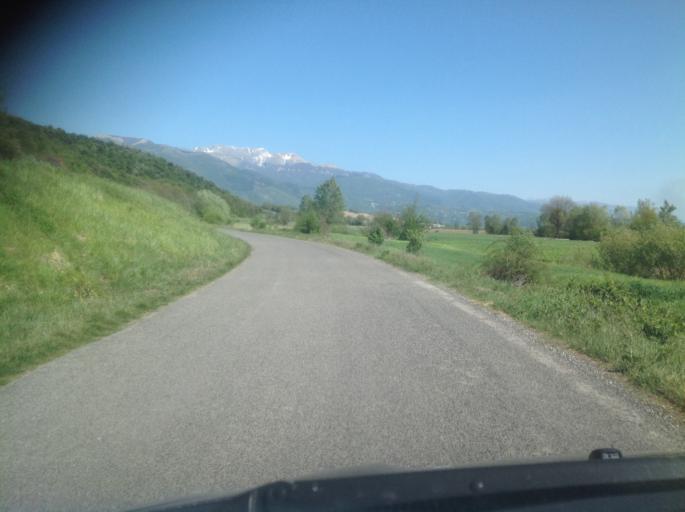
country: IT
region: Latium
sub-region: Provincia di Rieti
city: Colli sul Velino
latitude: 42.4927
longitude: 12.7928
